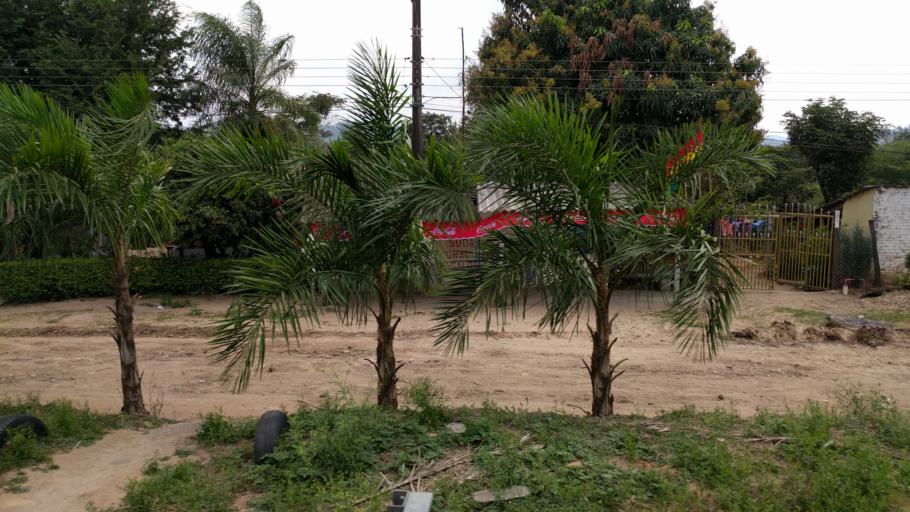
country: BO
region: Santa Cruz
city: Limoncito
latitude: -18.0113
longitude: -63.3932
